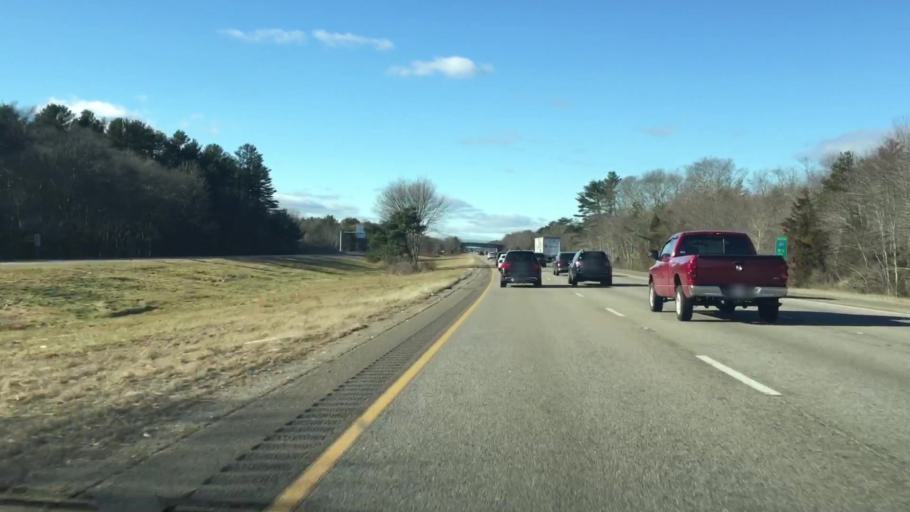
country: US
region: Massachusetts
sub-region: Bristol County
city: Norton Center
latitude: 41.9922
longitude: -71.1754
